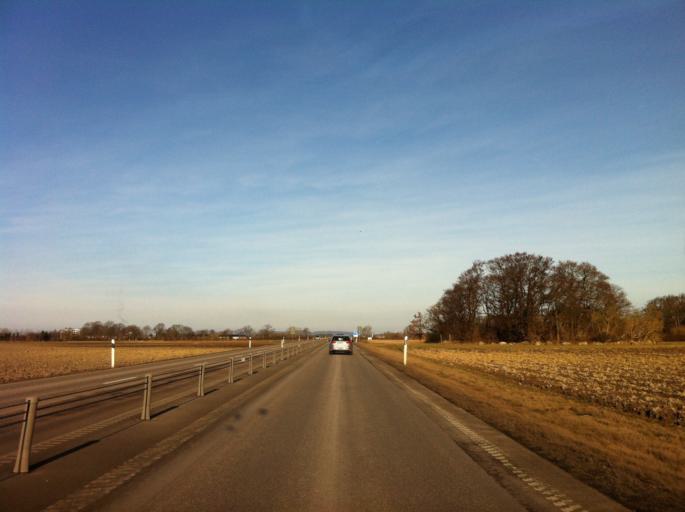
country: SE
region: Skane
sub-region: Helsingborg
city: Odakra
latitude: 56.1079
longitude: 12.7141
